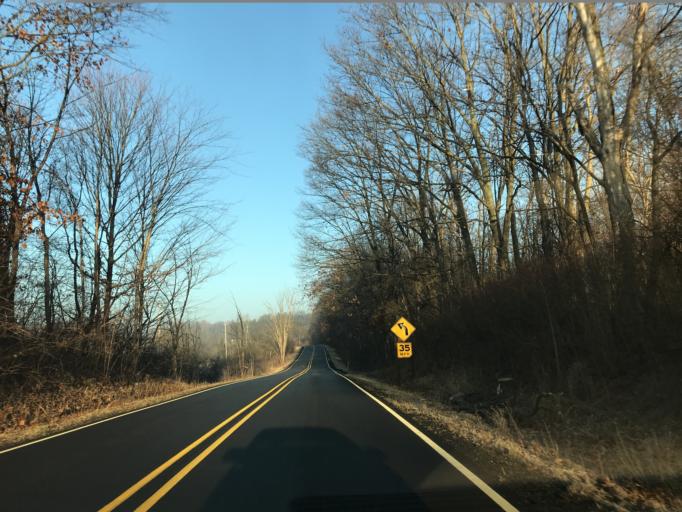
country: US
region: Michigan
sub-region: Ingham County
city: Leslie
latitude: 42.4335
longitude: -84.5356
